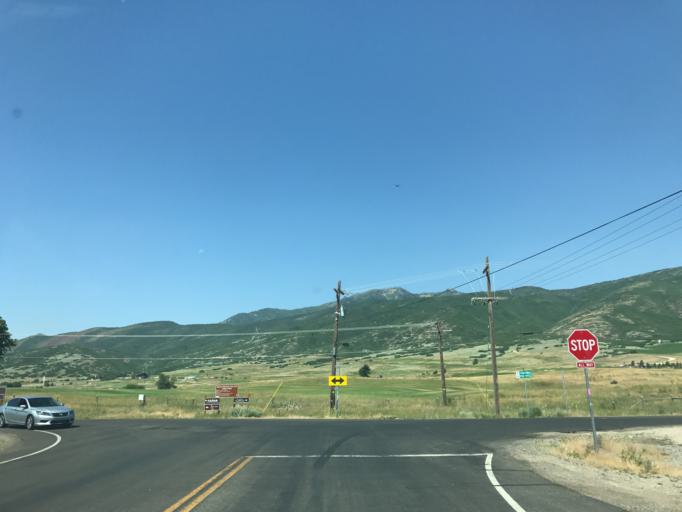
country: US
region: Utah
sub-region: Wasatch County
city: Midway
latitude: 40.4867
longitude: -111.4817
